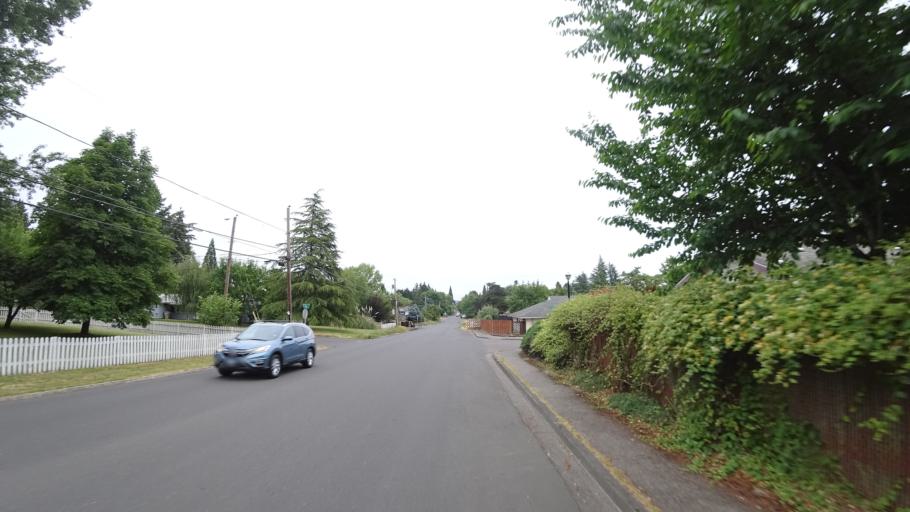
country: US
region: Oregon
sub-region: Washington County
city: Aloha
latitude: 45.5004
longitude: -122.8786
